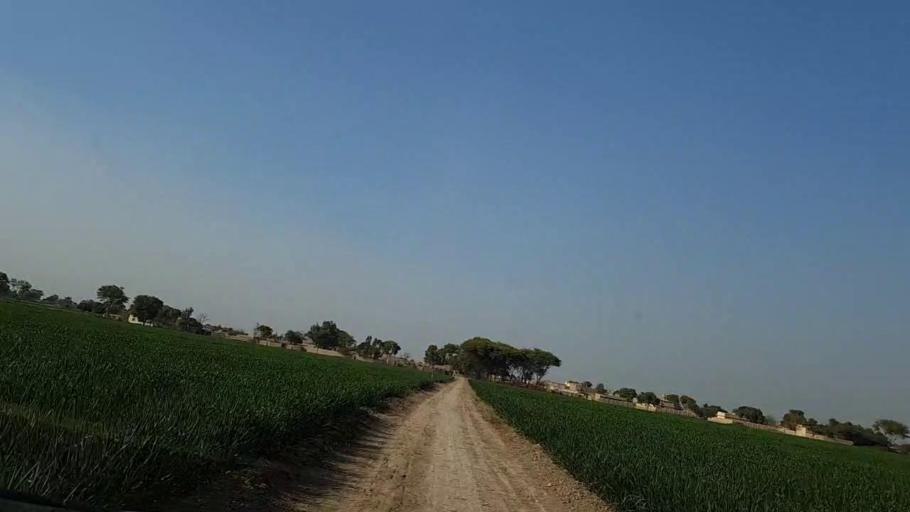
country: PK
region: Sindh
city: Sakrand
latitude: 26.1226
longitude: 68.2395
